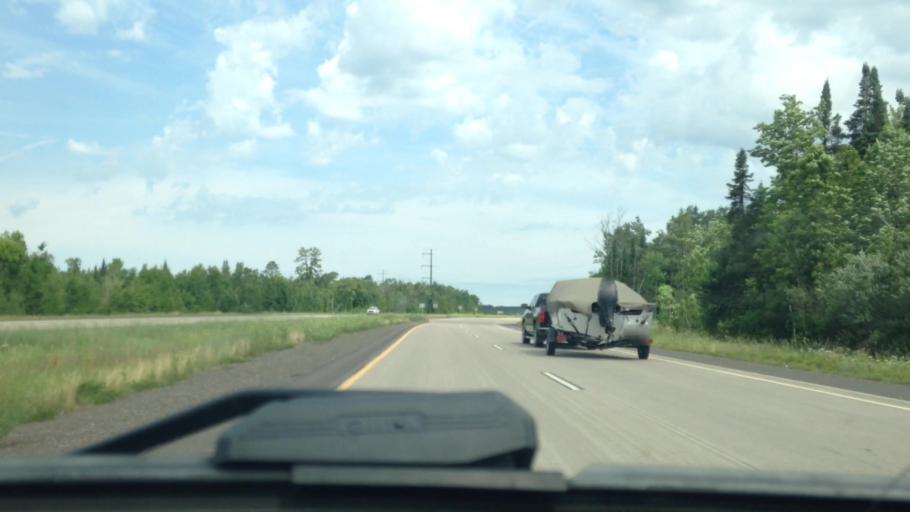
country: US
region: Wisconsin
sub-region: Douglas County
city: Lake Nebagamon
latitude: 46.2523
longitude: -91.8017
